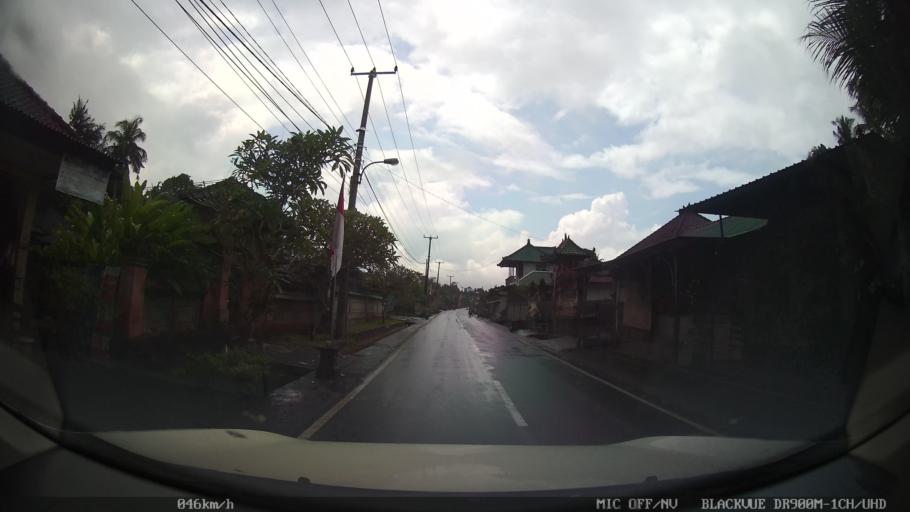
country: ID
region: Bali
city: Banjar Teguan
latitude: -8.5079
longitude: 115.2302
